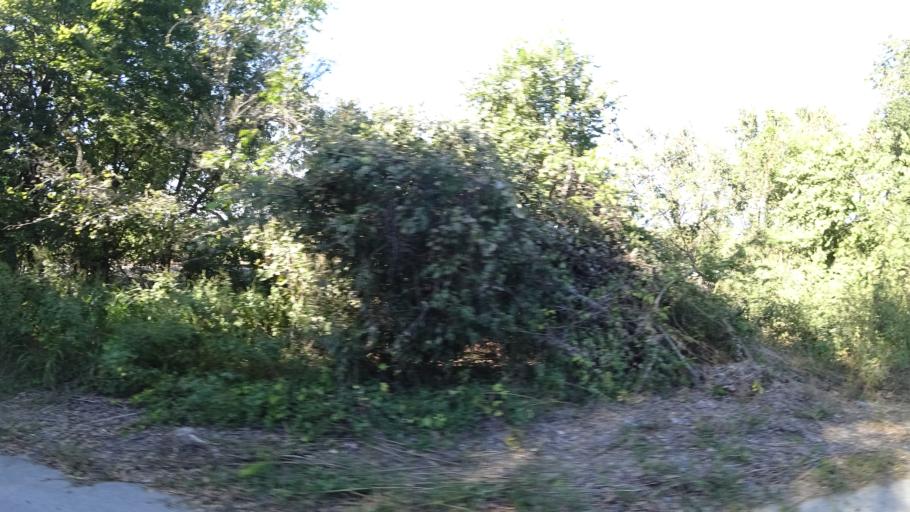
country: US
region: Texas
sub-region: Travis County
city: Austin
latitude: 30.2635
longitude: -97.6630
